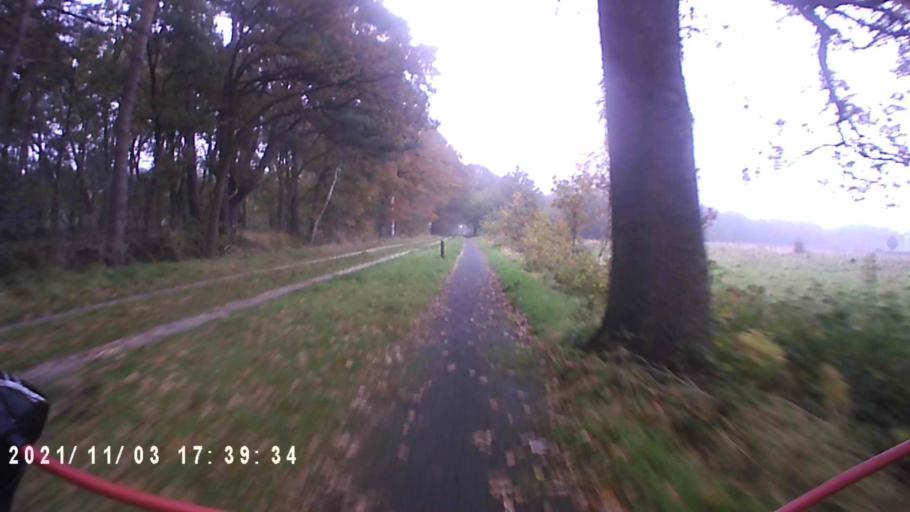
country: NL
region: Drenthe
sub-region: Gemeente Westerveld
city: Dwingeloo
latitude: 52.8670
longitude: 6.2955
